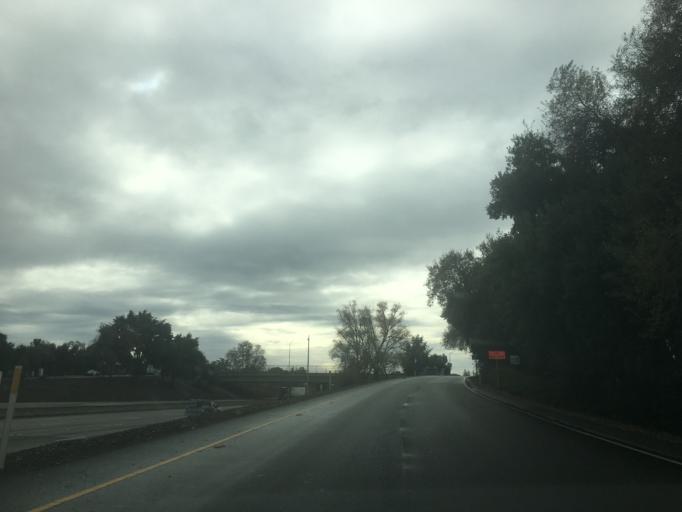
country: US
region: California
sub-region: Sacramento County
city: Sacramento
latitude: 38.5423
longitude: -121.5087
